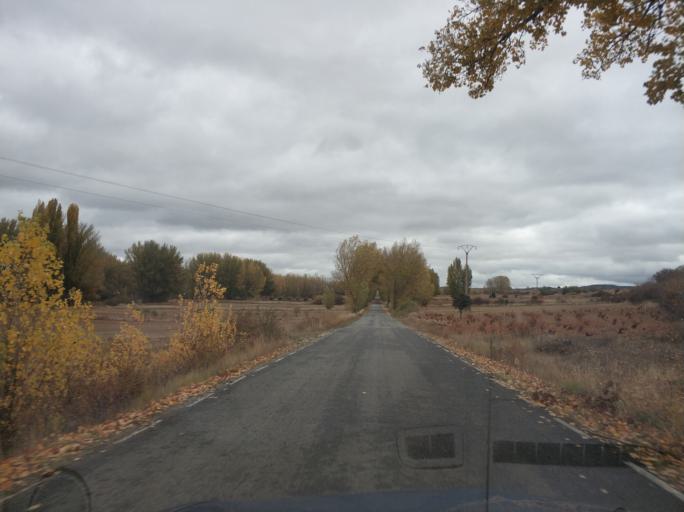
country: ES
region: Castille and Leon
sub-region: Provincia de Soria
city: San Esteban de Gormaz
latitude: 41.5831
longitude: -3.1978
